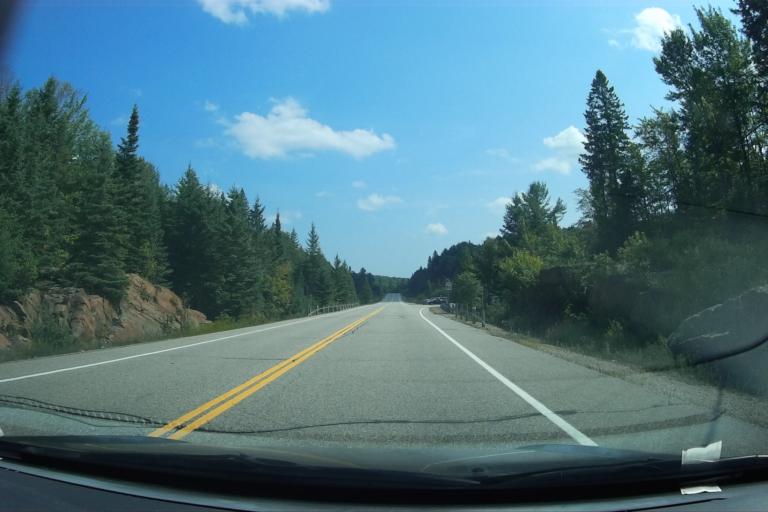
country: CA
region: Ontario
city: Huntsville
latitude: 45.5651
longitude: -78.5547
